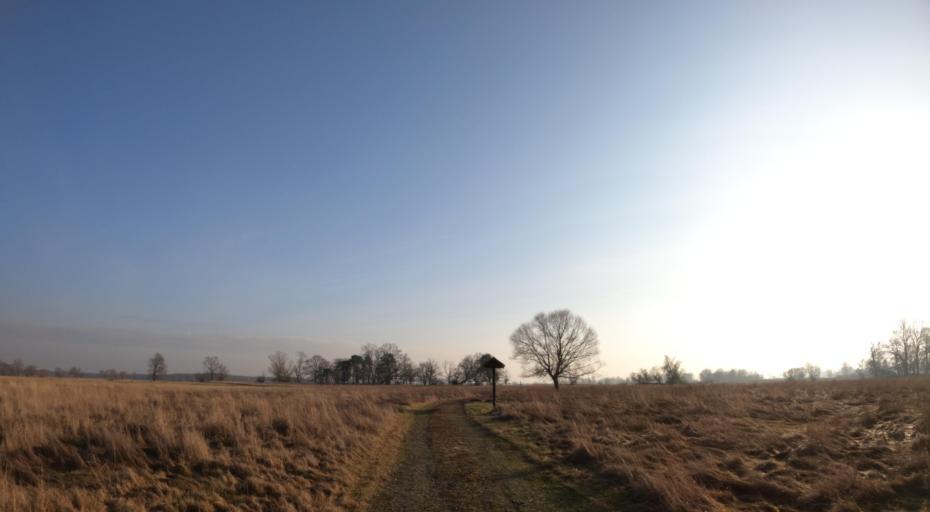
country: DE
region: Brandenburg
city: Zechin
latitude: 52.6585
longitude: 14.4895
